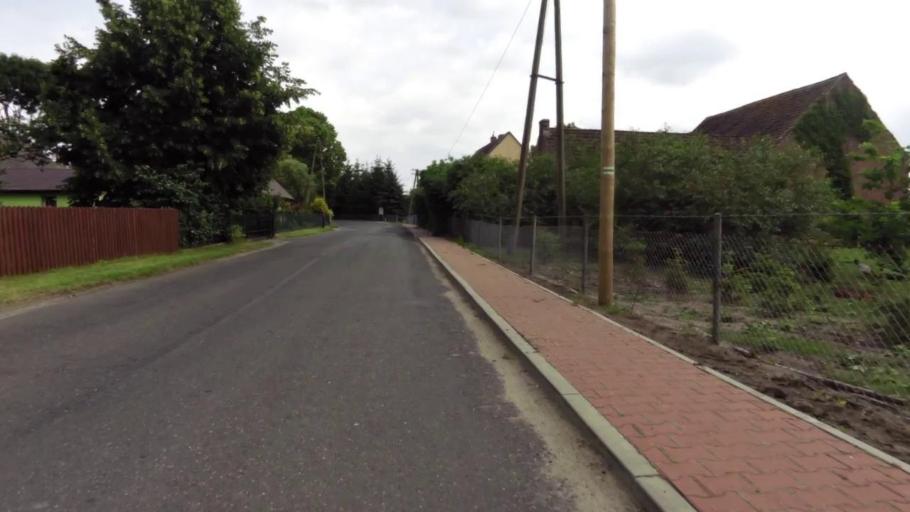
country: PL
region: West Pomeranian Voivodeship
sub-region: Powiat goleniowski
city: Stepnica
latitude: 53.6636
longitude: 14.5958
